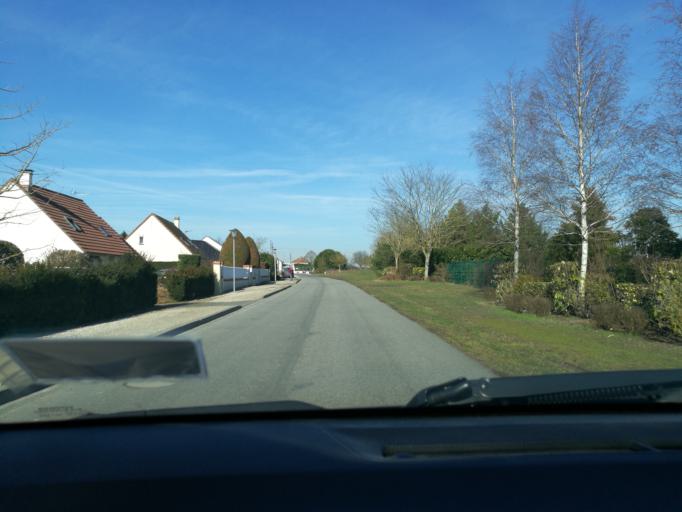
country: FR
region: Centre
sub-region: Departement du Loiret
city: Saint-Ay
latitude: 47.8644
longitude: 1.7563
